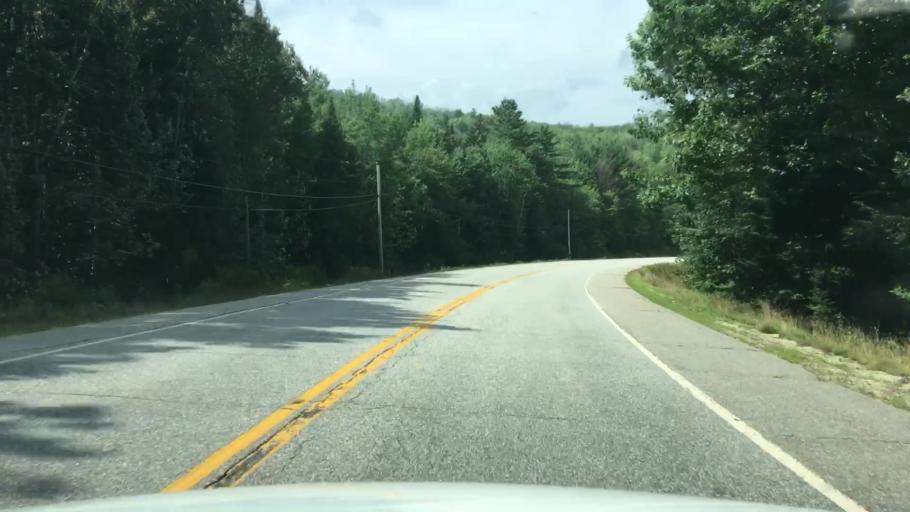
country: US
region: Maine
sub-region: Oxford County
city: Rumford
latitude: 44.5490
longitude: -70.7071
